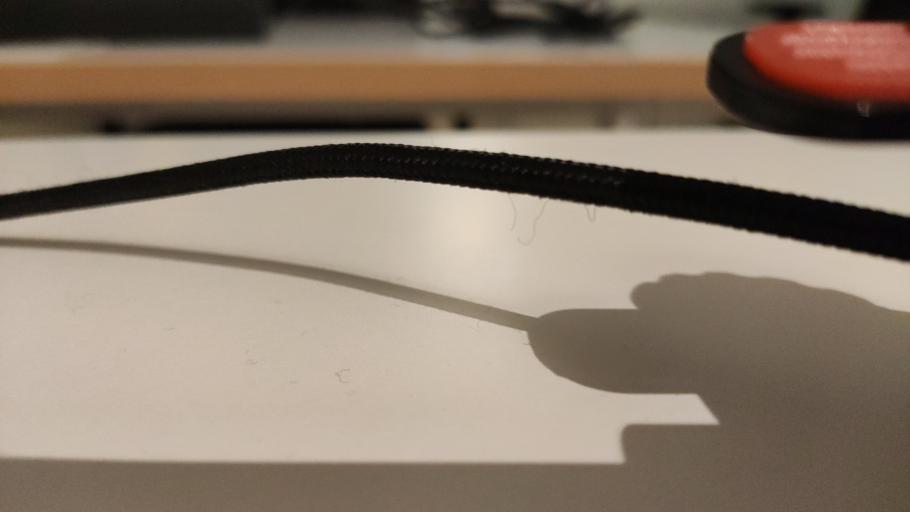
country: RU
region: Moskovskaya
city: Dmitrov
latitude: 56.3645
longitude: 37.5396
